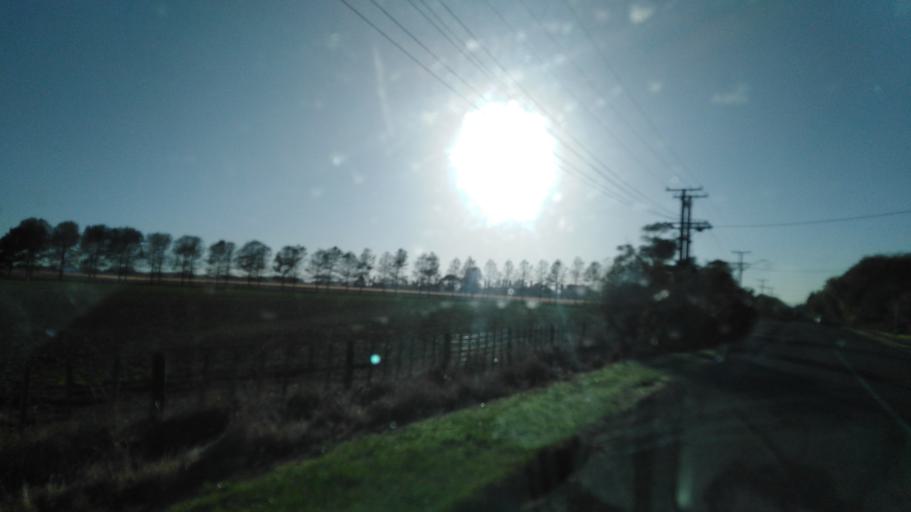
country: NZ
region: Manawatu-Wanganui
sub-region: Rangitikei District
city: Bulls
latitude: -40.0639
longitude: 175.3847
